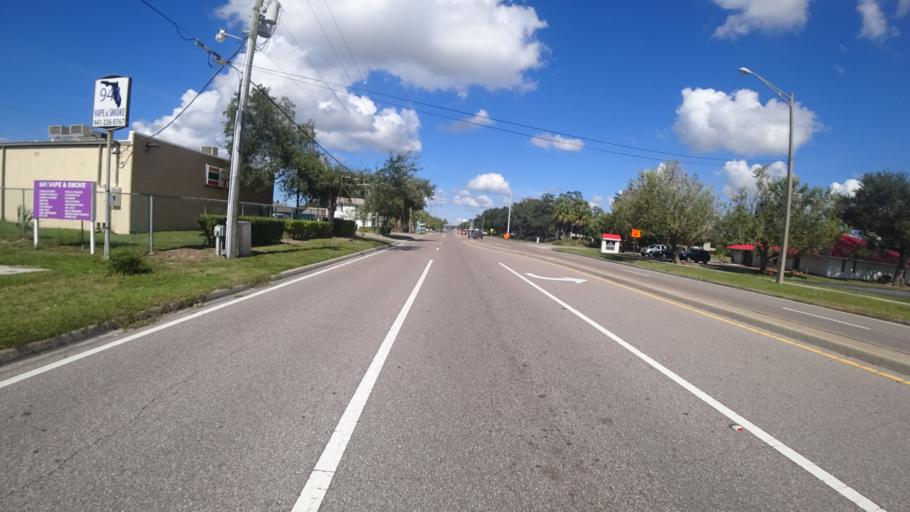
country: US
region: Florida
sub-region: Manatee County
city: South Bradenton
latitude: 27.4640
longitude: -82.6205
